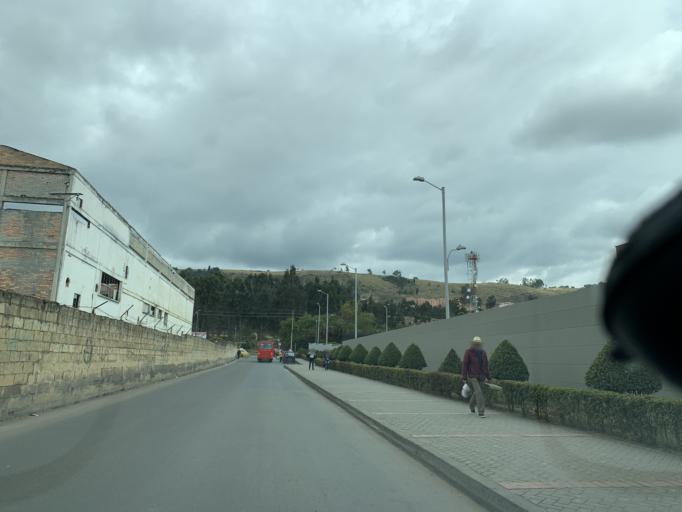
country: CO
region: Boyaca
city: Tunja
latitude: 5.5567
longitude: -73.3492
